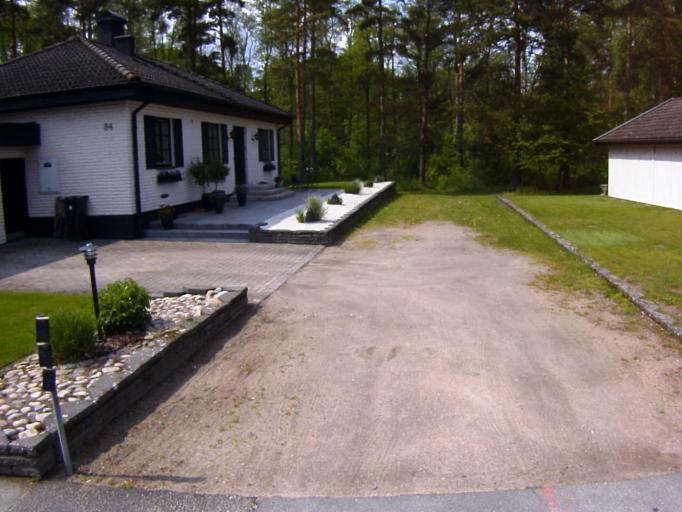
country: SE
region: Skane
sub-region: Kristianstads Kommun
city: Degeberga
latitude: 55.8235
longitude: 14.0859
